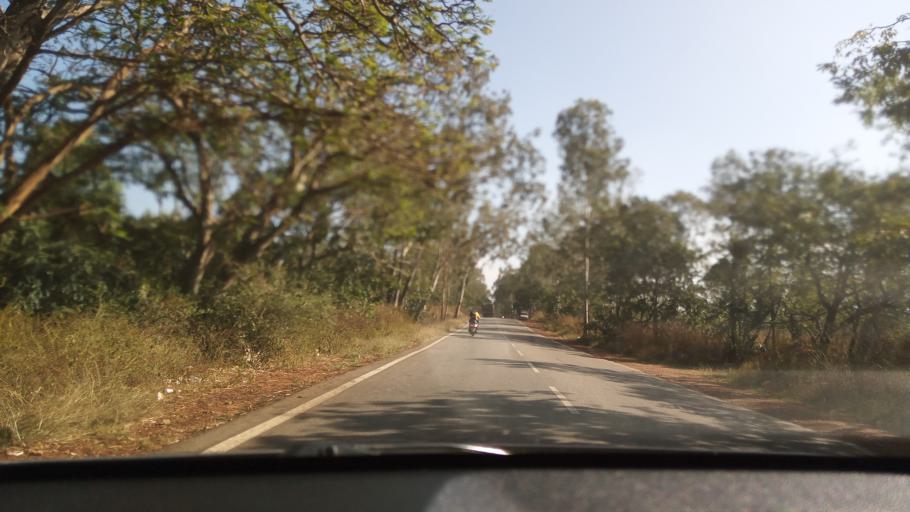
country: IN
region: Karnataka
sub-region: Bangalore Rural
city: Vijayapura
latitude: 13.2843
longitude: 77.7694
